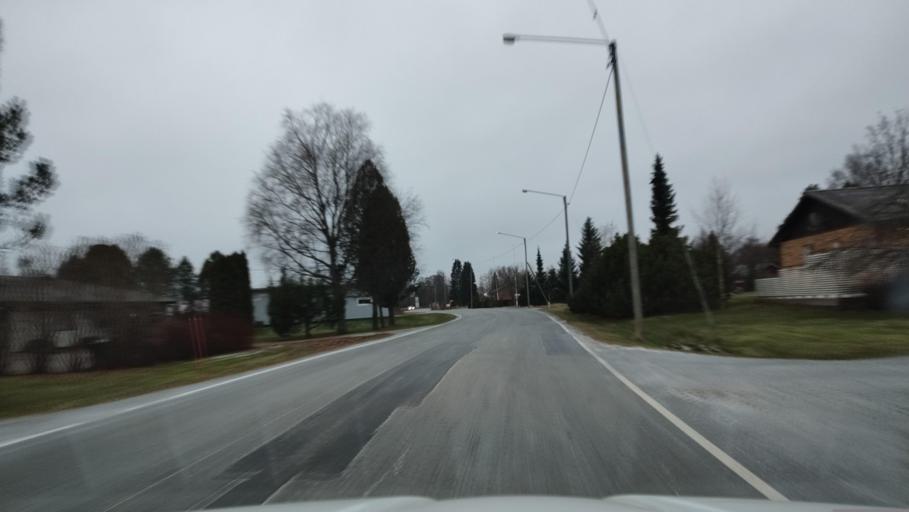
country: FI
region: Southern Ostrobothnia
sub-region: Suupohja
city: Karijoki
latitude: 62.2341
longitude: 21.6500
